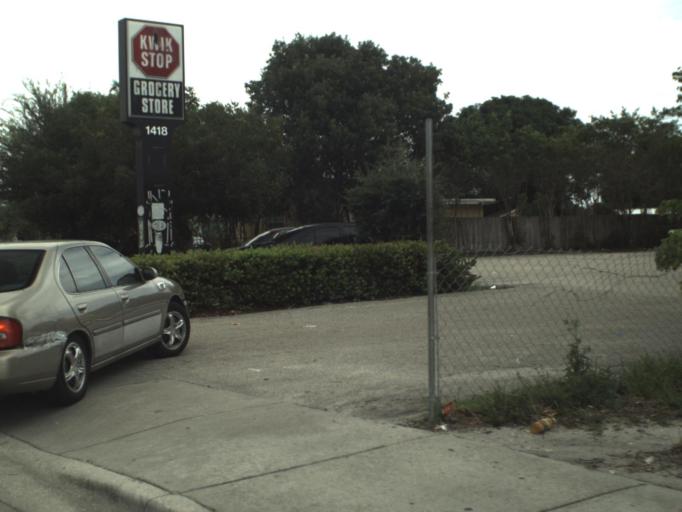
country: US
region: Florida
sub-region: Palm Beach County
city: Lantana
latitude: 26.5979
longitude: -80.0553
